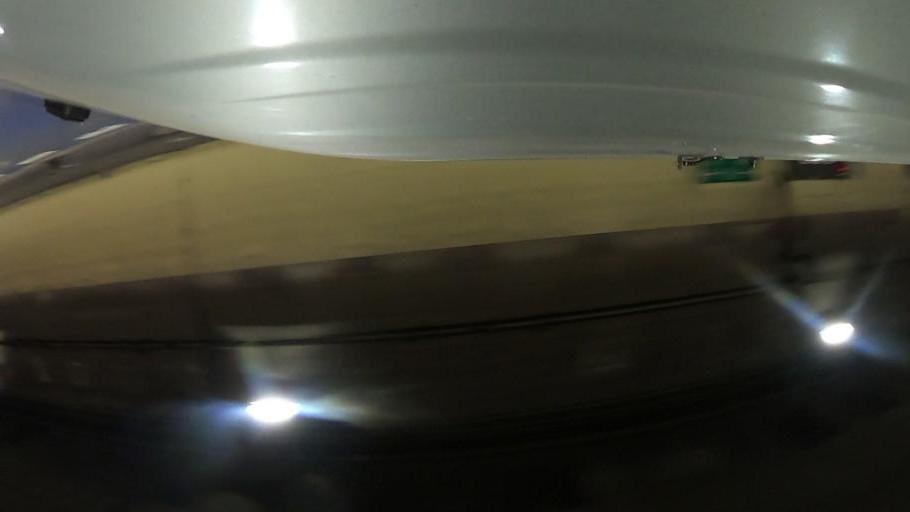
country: JP
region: Kanagawa
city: Yokohama
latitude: 35.4603
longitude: 139.6243
